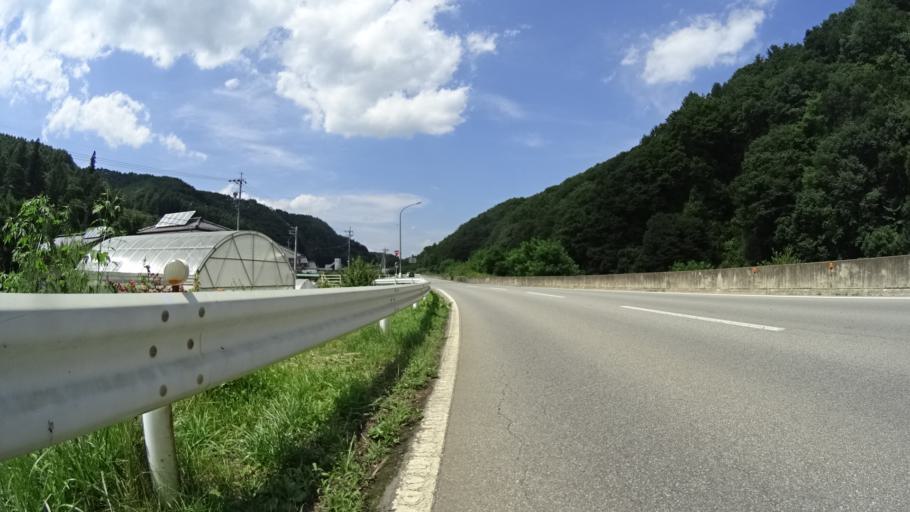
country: JP
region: Nagano
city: Saku
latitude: 36.0722
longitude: 138.4967
